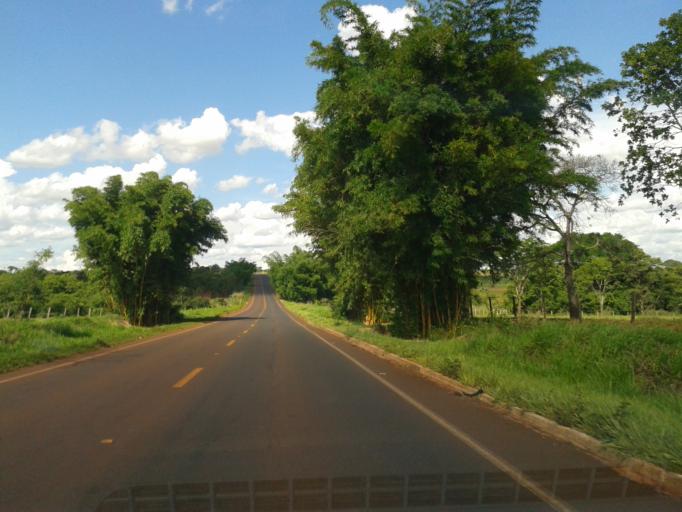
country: BR
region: Minas Gerais
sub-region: Iturama
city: Iturama
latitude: -19.6844
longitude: -50.1377
